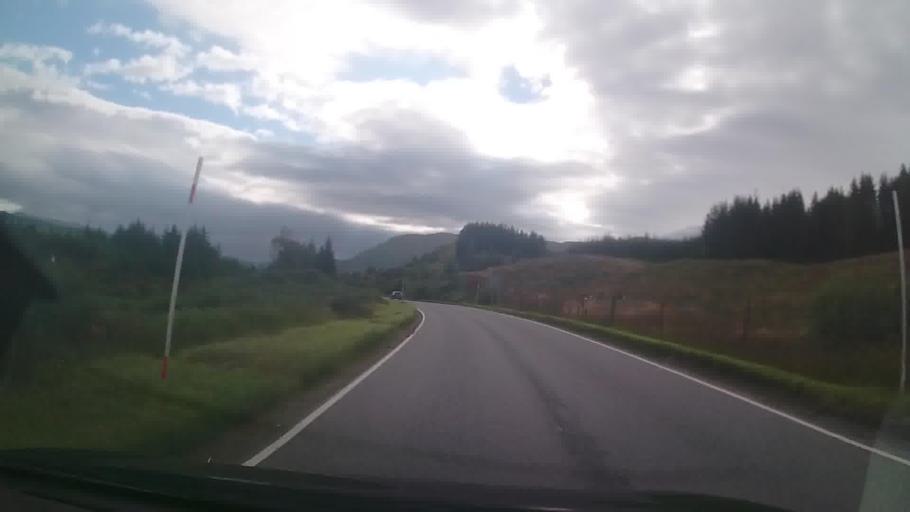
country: GB
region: Scotland
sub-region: Argyll and Bute
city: Garelochhead
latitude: 56.3288
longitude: -5.0746
